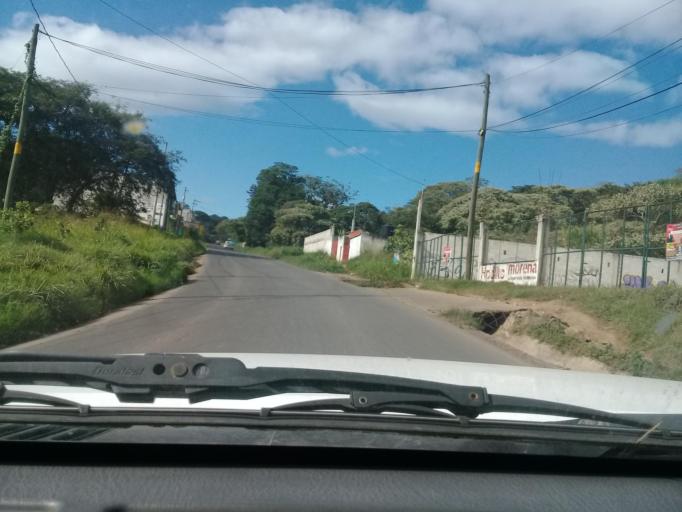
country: MX
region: Veracruz
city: El Castillo
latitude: 19.5489
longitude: -96.8798
